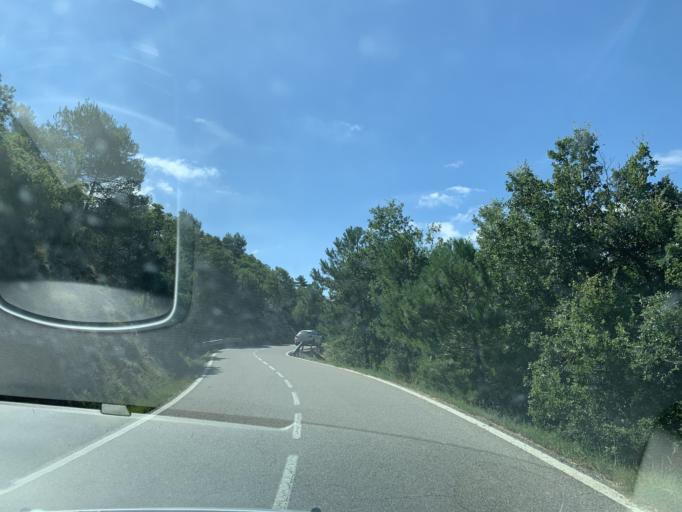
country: ES
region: Catalonia
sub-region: Provincia de Tarragona
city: Conesa
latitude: 41.5449
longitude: 1.3257
